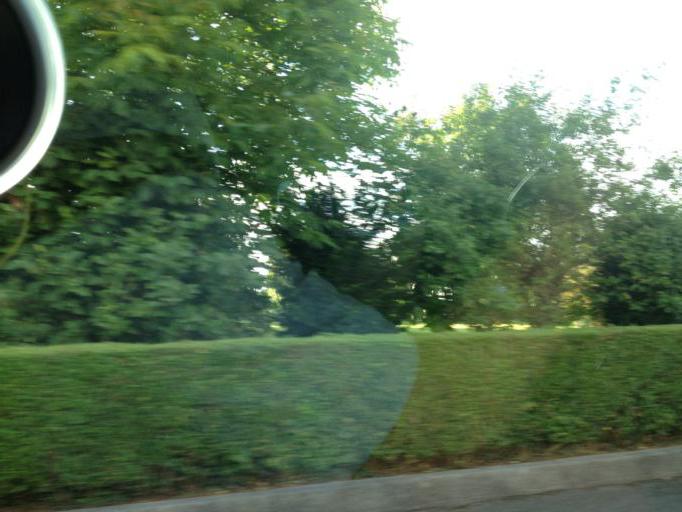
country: DE
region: Saarland
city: Neunkirchen
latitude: 49.3663
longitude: 7.1678
